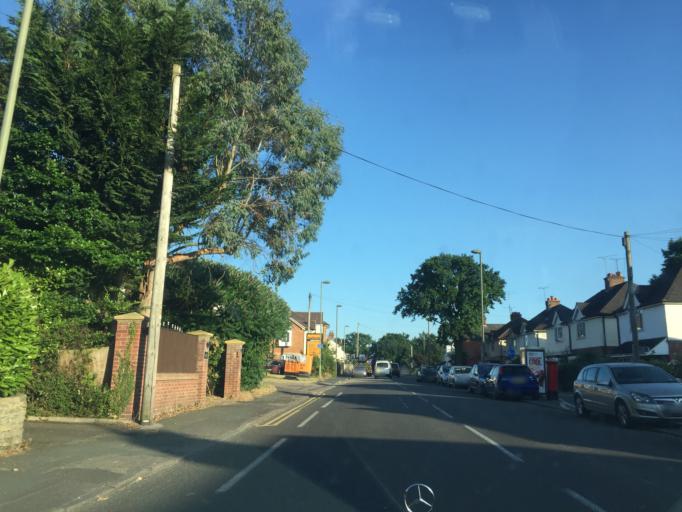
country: GB
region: England
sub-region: Surrey
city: Camberley
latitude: 51.3319
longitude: -0.7575
